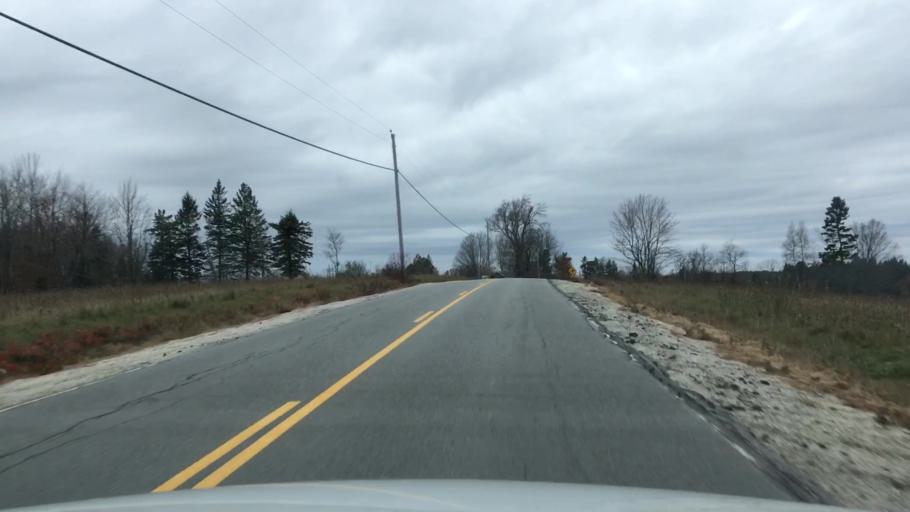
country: US
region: Maine
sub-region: Hancock County
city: Penobscot
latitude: 44.4402
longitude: -68.6352
